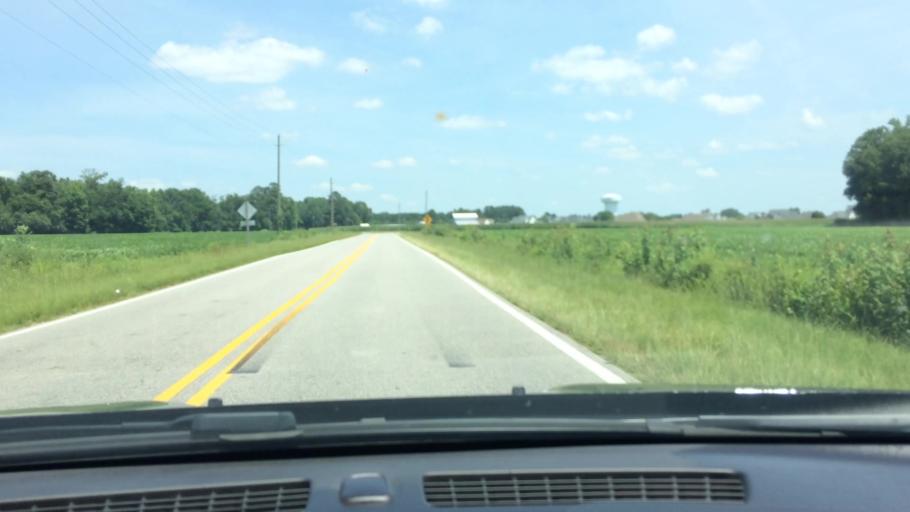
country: US
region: North Carolina
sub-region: Pitt County
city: Windsor
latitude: 35.5245
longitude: -77.3064
